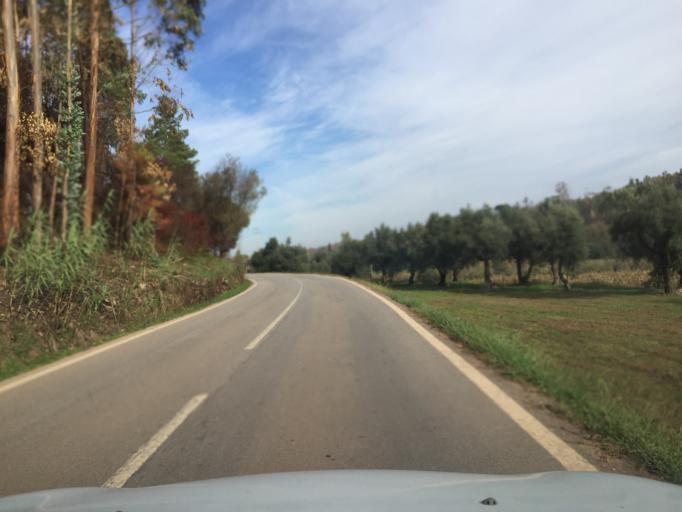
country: PT
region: Aveiro
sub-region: Anadia
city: Anadia
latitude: 40.4166
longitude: -8.4135
